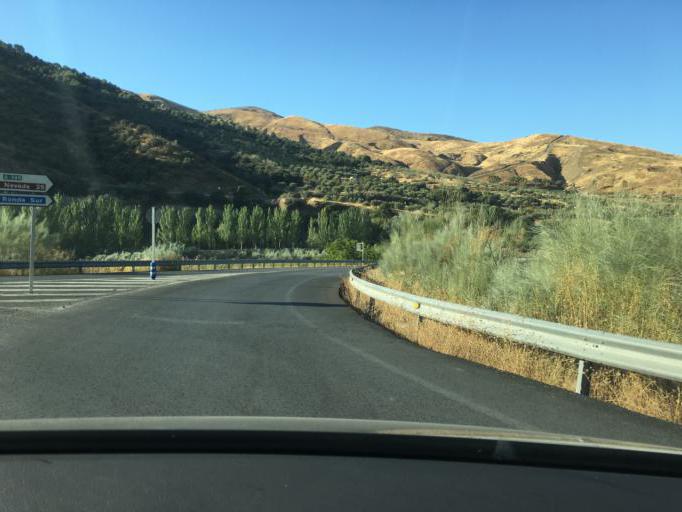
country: ES
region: Andalusia
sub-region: Provincia de Granada
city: Cenes de la Vega
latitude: 37.1574
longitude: -3.5300
